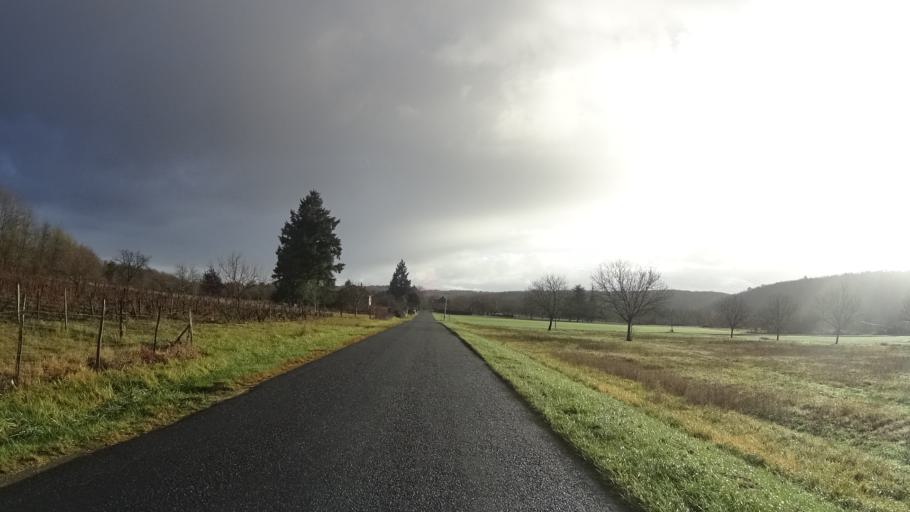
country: FR
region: Aquitaine
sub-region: Departement de la Dordogne
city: Sorges
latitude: 45.2751
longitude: 0.9285
